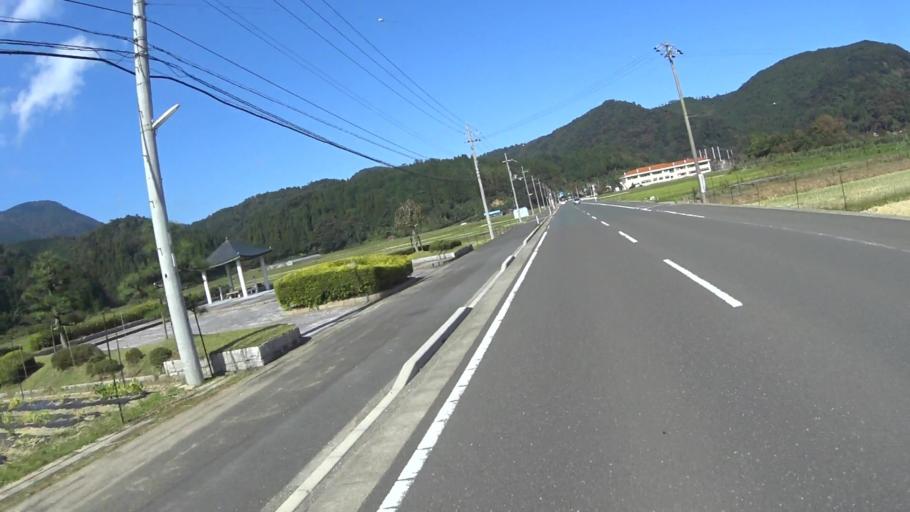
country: JP
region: Kyoto
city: Miyazu
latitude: 35.7248
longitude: 135.2549
